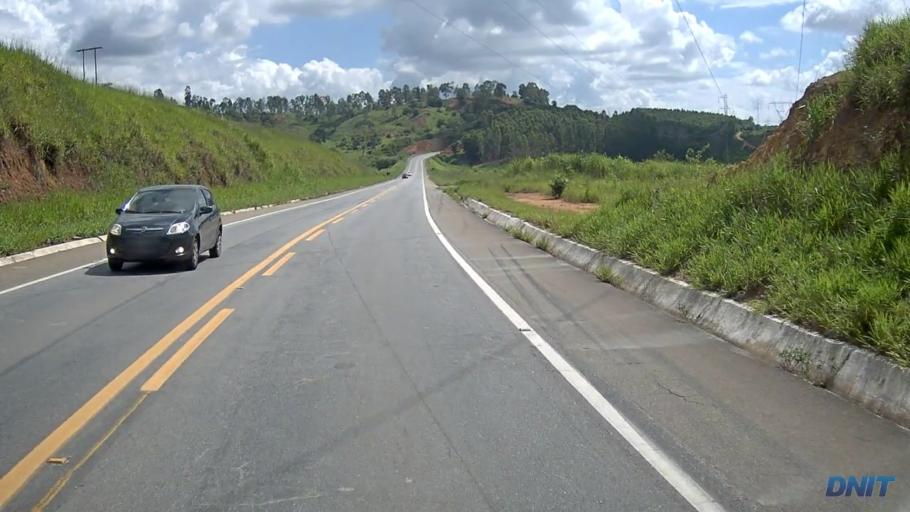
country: BR
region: Minas Gerais
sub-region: Belo Oriente
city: Belo Oriente
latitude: -19.0888
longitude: -42.1887
